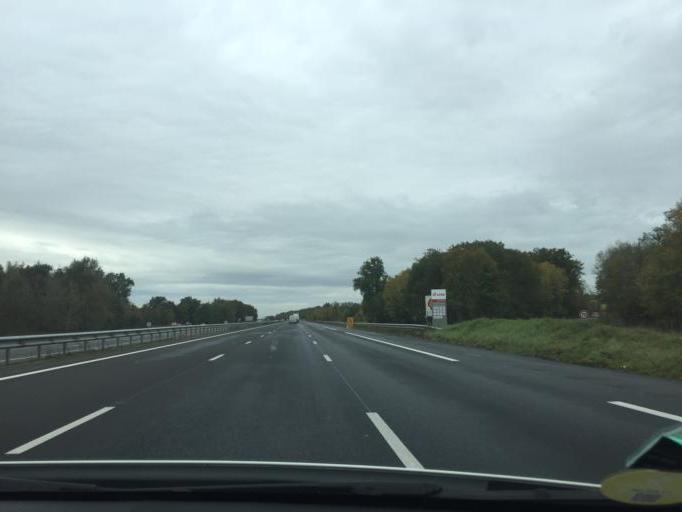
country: FR
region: Ile-de-France
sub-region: Departement de Seine-et-Marne
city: Montereau-Fault-Yonne
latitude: 48.4237
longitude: 2.9350
